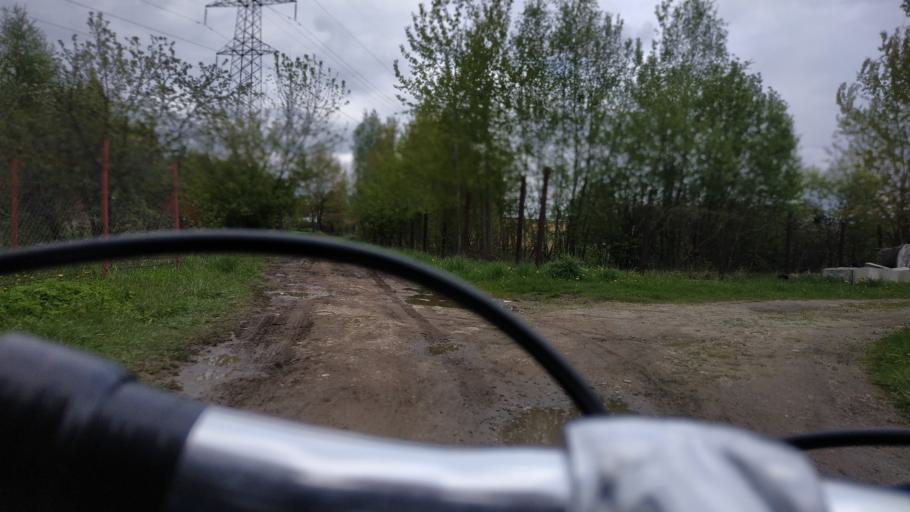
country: RU
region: Moskovskaya
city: Rechitsy
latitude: 55.6197
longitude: 38.5378
